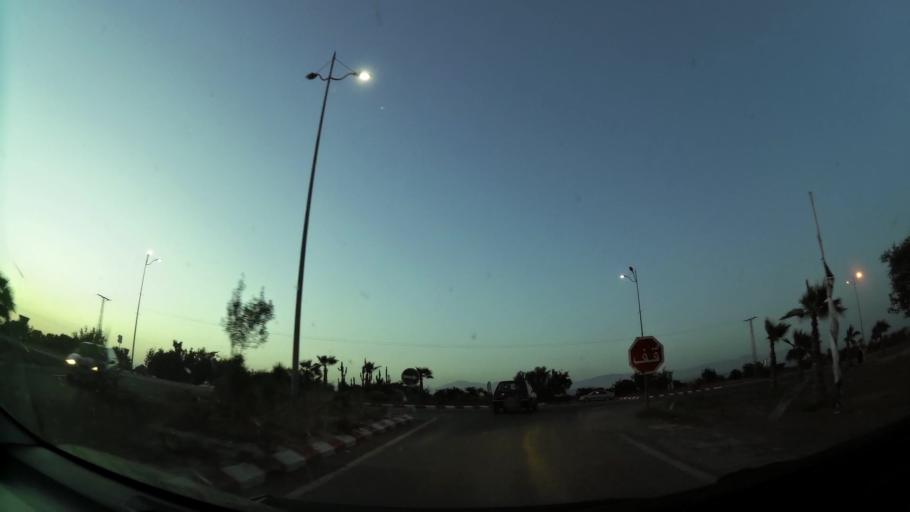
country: MA
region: Souss-Massa-Draa
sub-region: Inezgane-Ait Mellou
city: Inezgane
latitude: 30.3864
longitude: -9.4856
